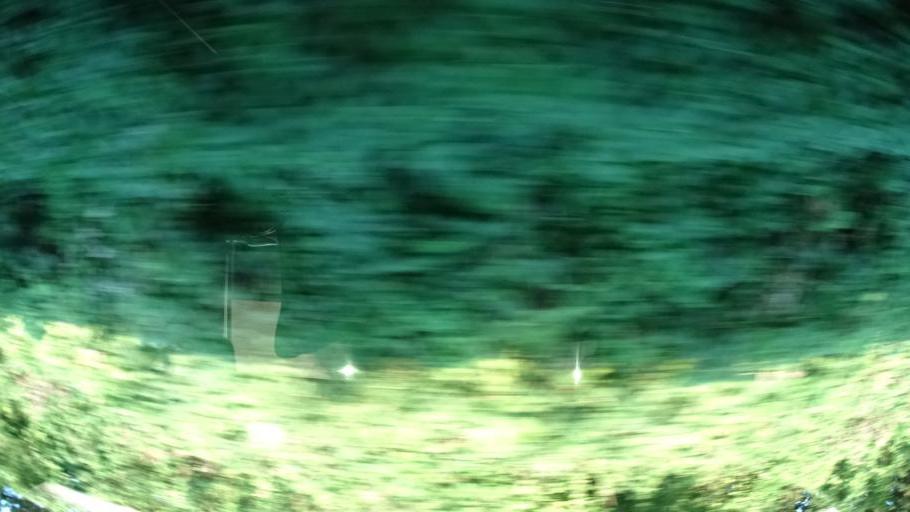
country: JP
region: Ibaraki
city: Naka
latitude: 36.0476
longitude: 140.1786
